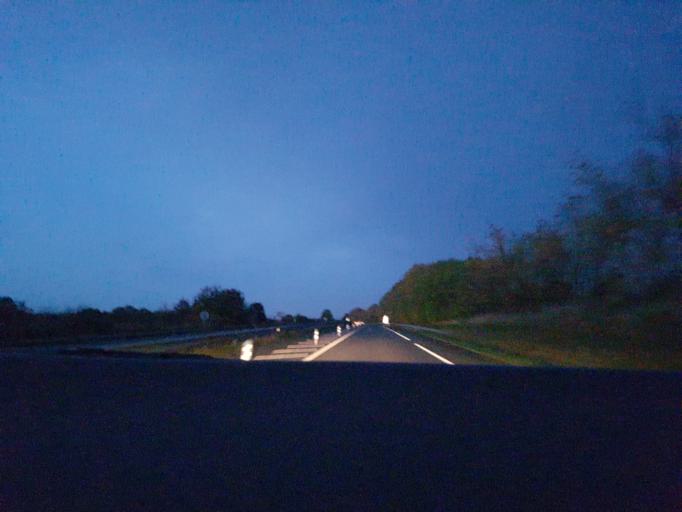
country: FR
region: Pays de la Loire
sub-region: Departement de la Mayenne
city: Martigne-sur-Mayenne
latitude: 48.1641
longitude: -0.6866
